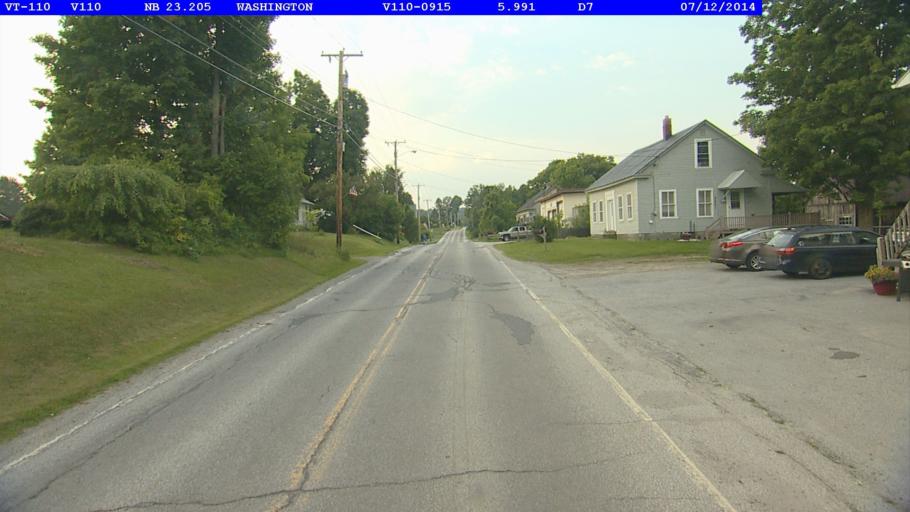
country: US
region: Vermont
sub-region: Washington County
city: South Barre
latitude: 44.1097
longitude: -72.4338
